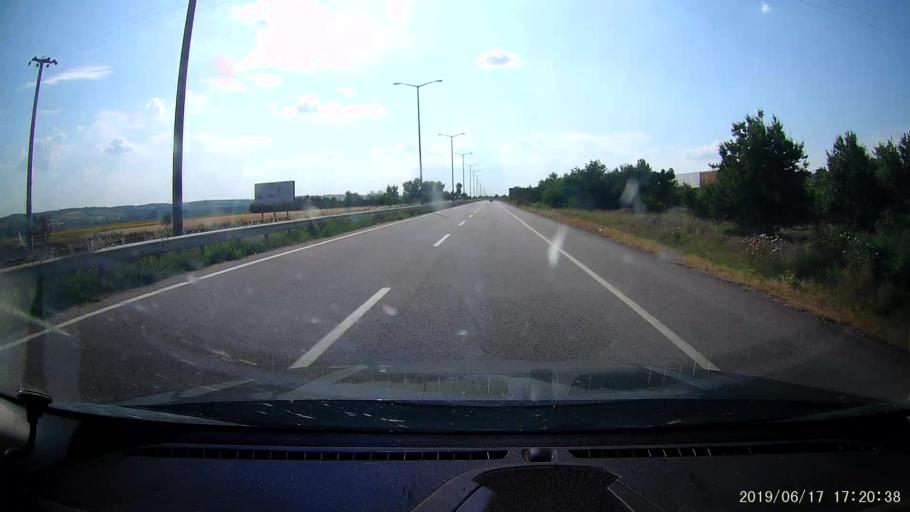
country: GR
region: East Macedonia and Thrace
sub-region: Nomos Evrou
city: Rizia
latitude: 41.7024
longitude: 26.4106
